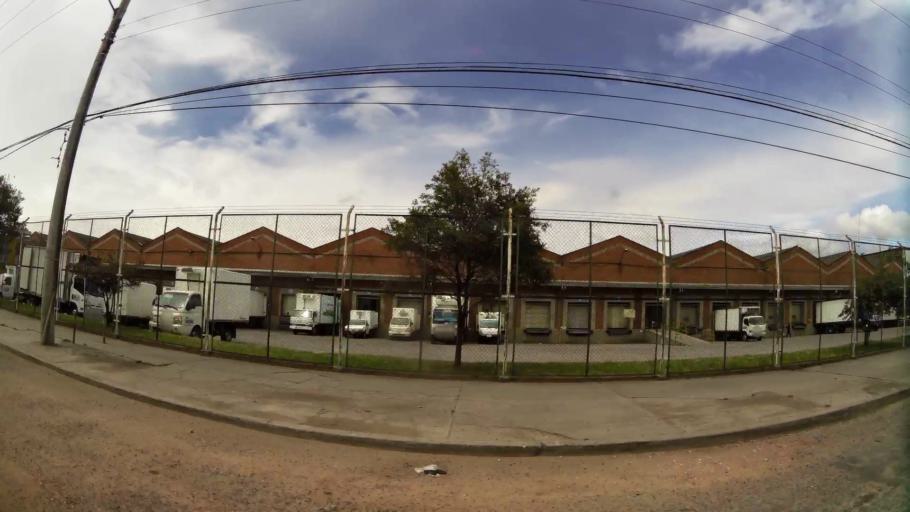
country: CO
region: Bogota D.C.
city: Bogota
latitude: 4.6313
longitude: -74.1230
